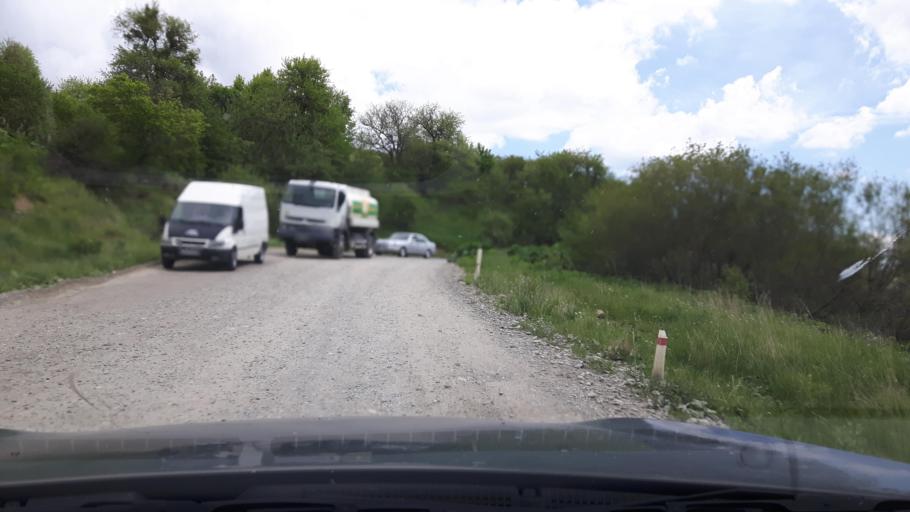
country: GE
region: Kakheti
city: Sagarejo
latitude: 41.8676
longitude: 45.2741
